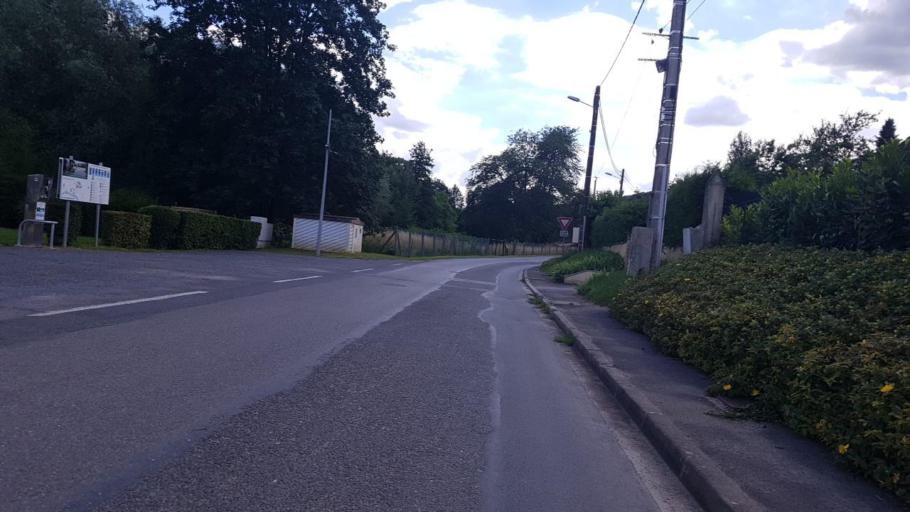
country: FR
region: Picardie
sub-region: Departement de l'Aisne
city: Crezancy
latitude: 49.0858
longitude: 3.5333
